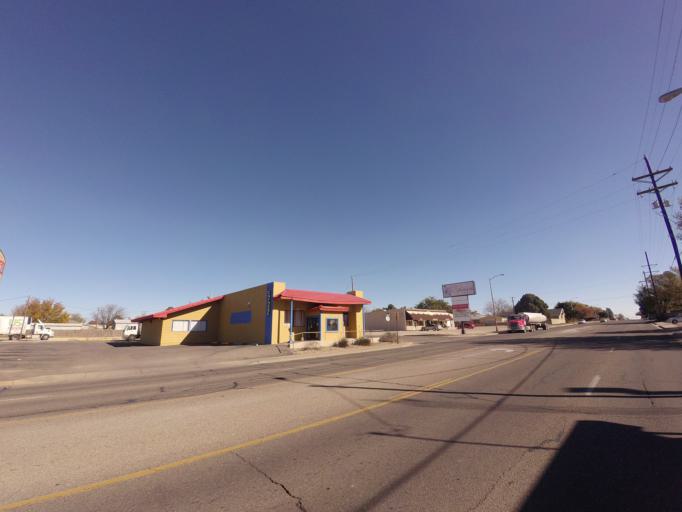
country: US
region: New Mexico
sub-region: Curry County
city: Clovis
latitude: 34.4193
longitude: -103.2044
